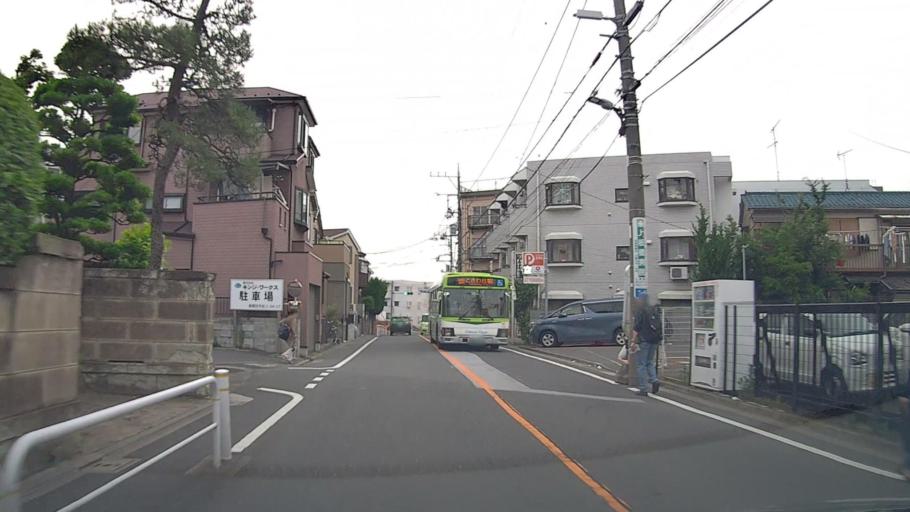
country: JP
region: Saitama
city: Shimotoda
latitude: 35.7656
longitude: 139.6787
